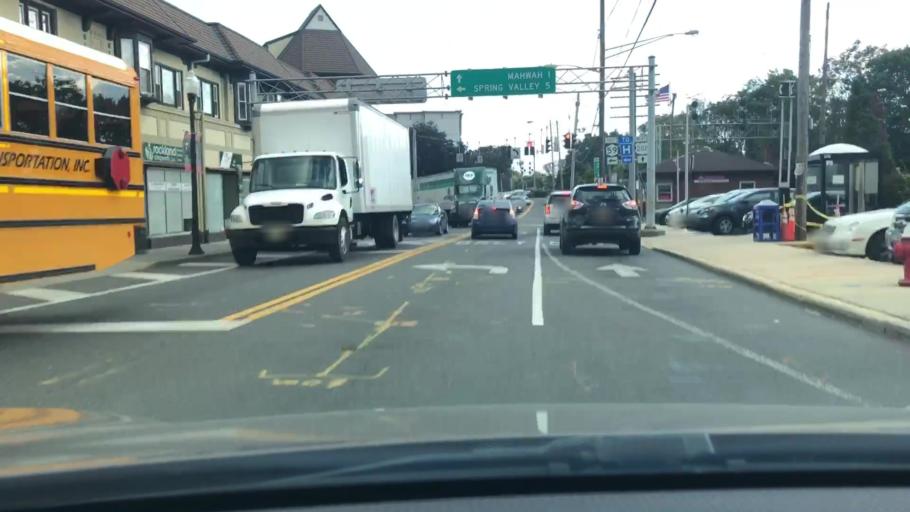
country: US
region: New York
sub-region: Rockland County
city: Suffern
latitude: 41.1169
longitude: -74.1549
